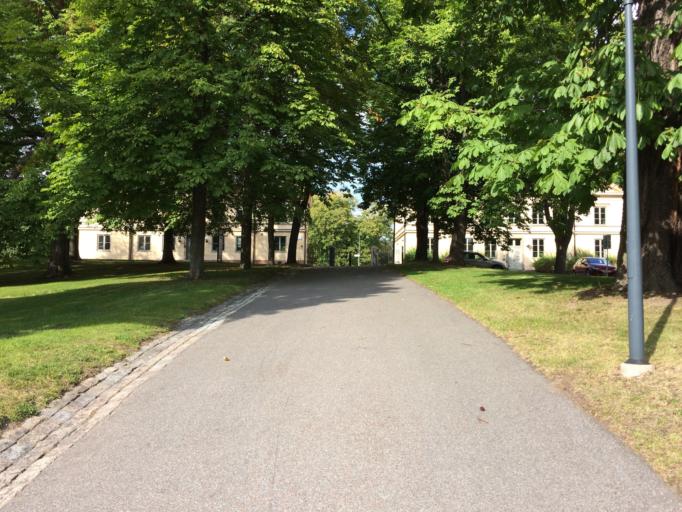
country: SE
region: Stockholm
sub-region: Stockholms Kommun
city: OEstermalm
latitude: 59.3249
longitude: 18.0866
